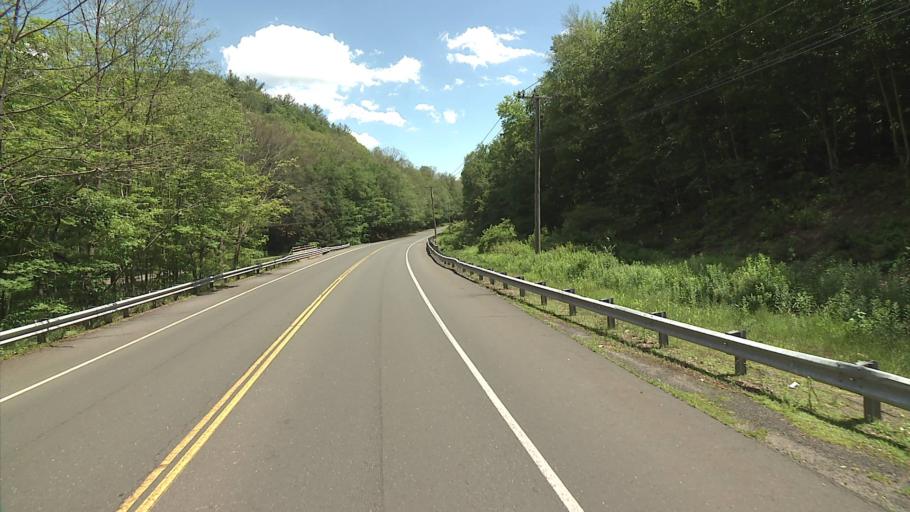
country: US
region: Connecticut
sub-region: New Haven County
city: Prospect
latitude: 41.4660
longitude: -72.9993
